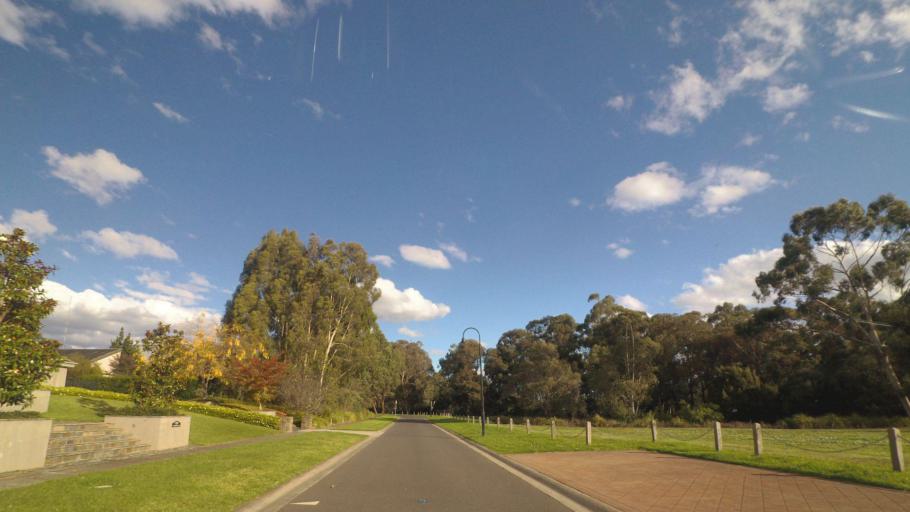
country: AU
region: Victoria
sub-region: Banyule
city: Lower Plenty
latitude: -37.7360
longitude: 145.1086
